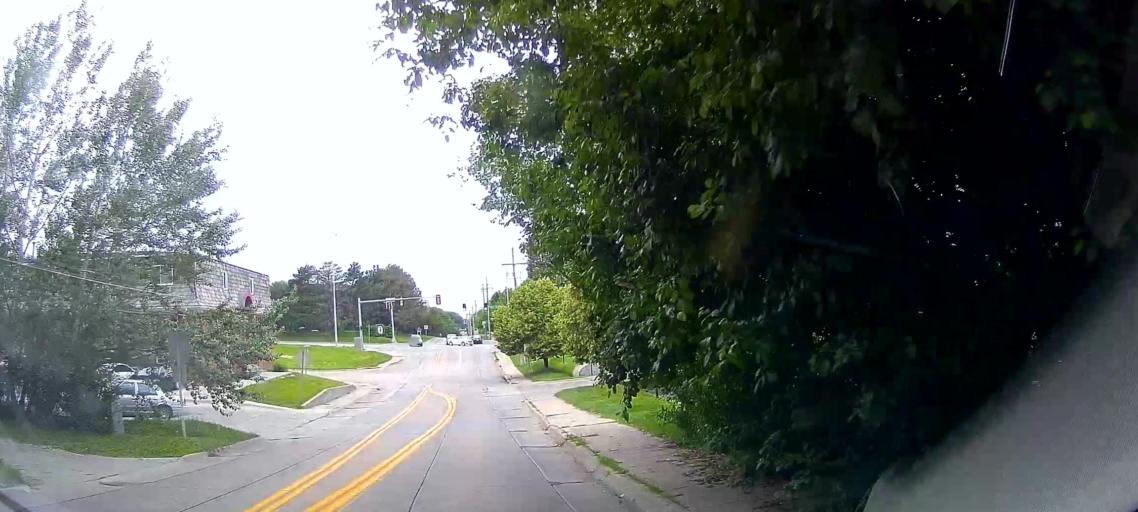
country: US
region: Nebraska
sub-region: Douglas County
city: Ralston
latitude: 41.2670
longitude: -96.0514
